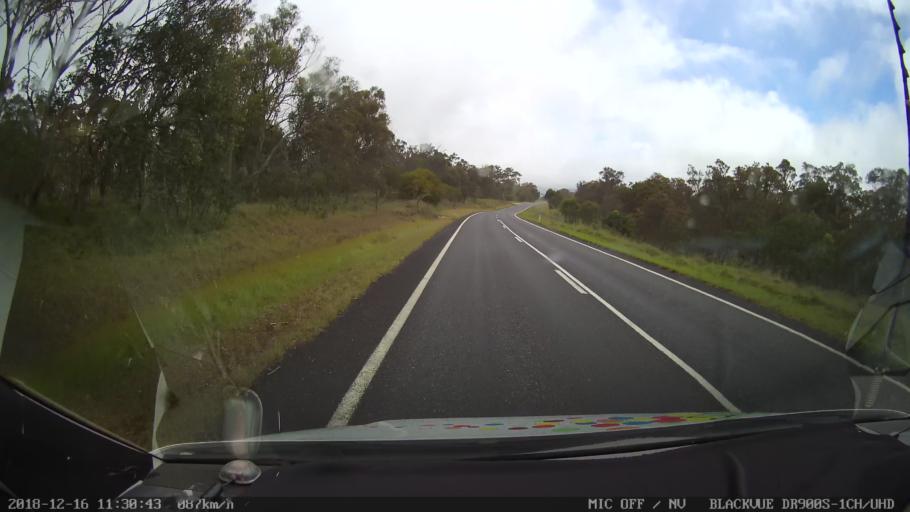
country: AU
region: New South Wales
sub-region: Tenterfield Municipality
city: Carrolls Creek
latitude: -29.0291
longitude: 152.1217
